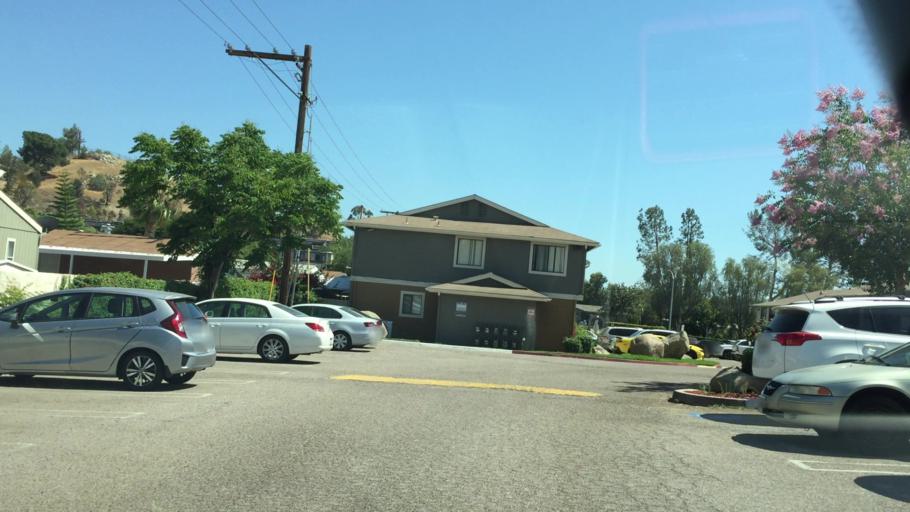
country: US
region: California
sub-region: San Diego County
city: Bostonia
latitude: 32.8202
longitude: -116.9554
